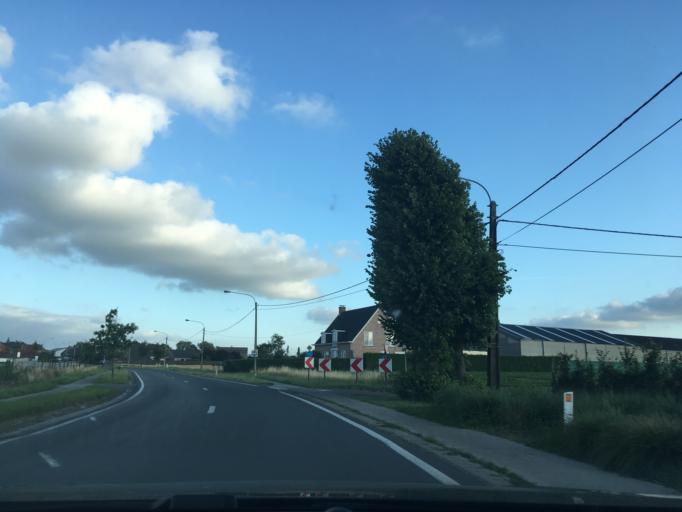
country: BE
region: Flanders
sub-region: Provincie West-Vlaanderen
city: Tielt
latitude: 51.0172
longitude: 3.3098
